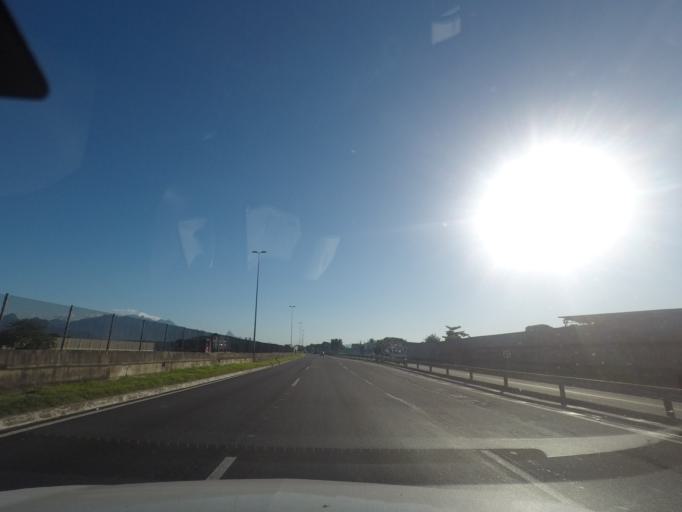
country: BR
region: Rio de Janeiro
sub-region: Duque De Caxias
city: Duque de Caxias
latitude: -22.6679
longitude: -43.2661
